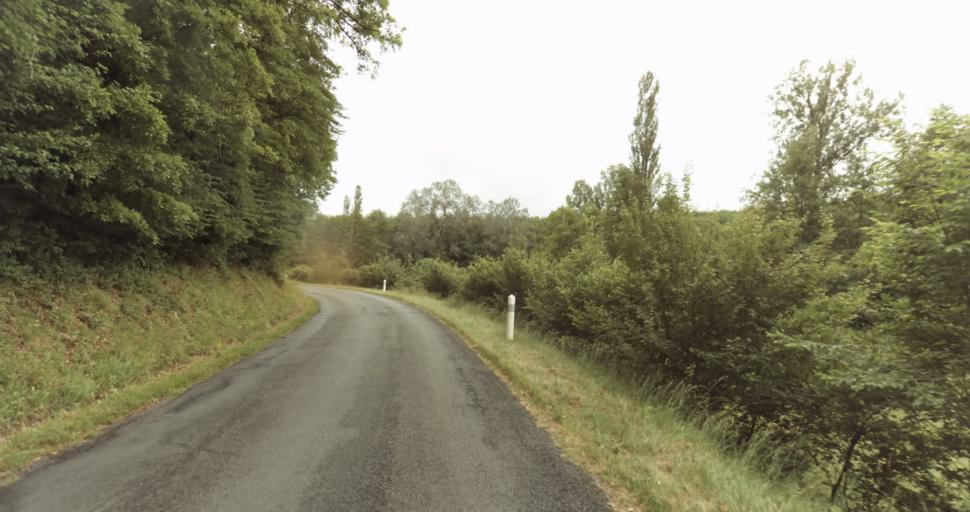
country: FR
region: Aquitaine
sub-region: Departement de la Dordogne
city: Beaumont-du-Perigord
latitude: 44.7561
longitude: 0.8098
